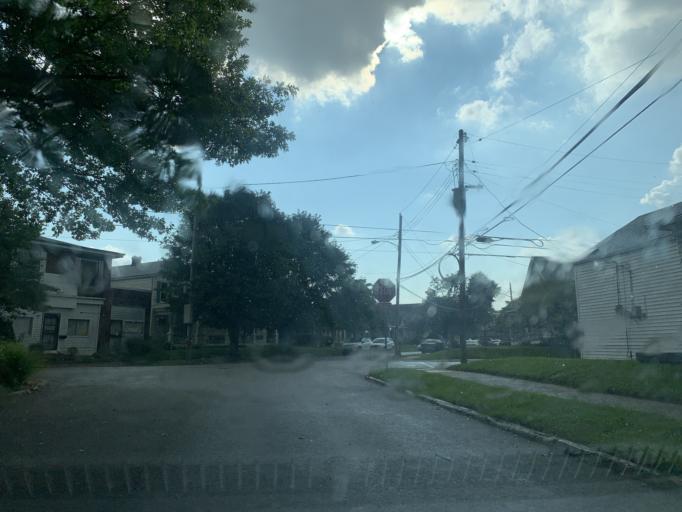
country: US
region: Kentucky
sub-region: Jefferson County
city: Audubon Park
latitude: 38.2155
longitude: -85.7488
